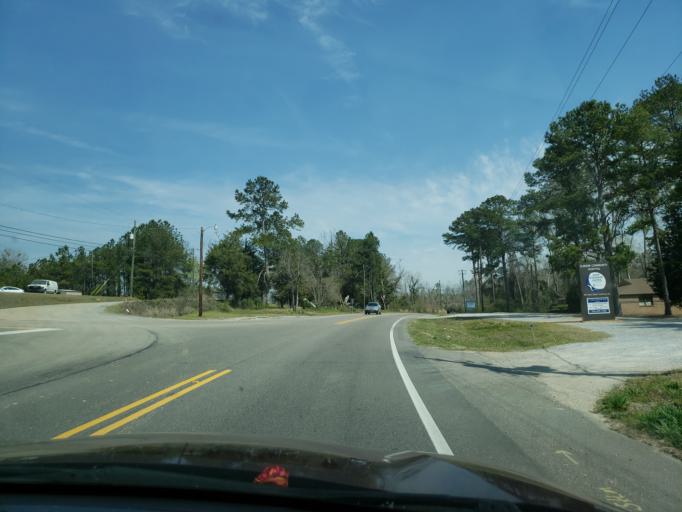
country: US
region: Alabama
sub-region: Elmore County
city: Wetumpka
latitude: 32.5517
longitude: -86.1856
